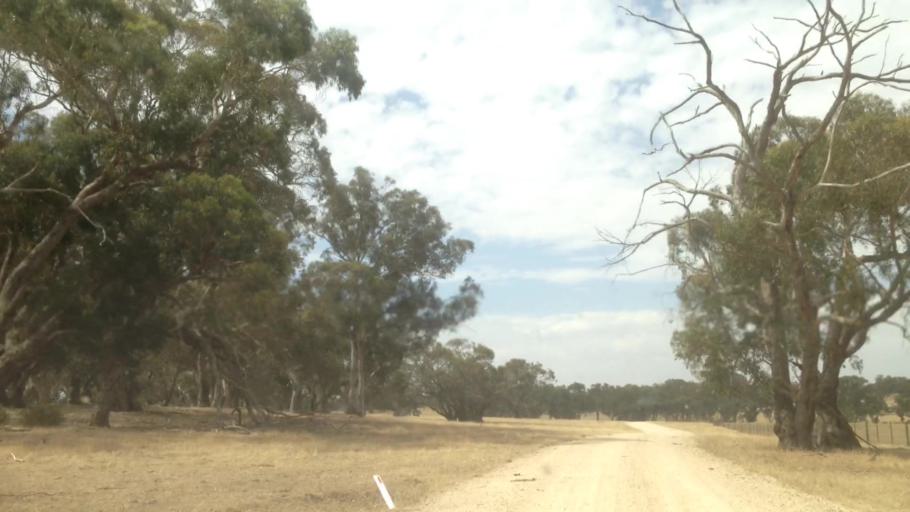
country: AU
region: South Australia
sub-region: Barossa
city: Williamstown
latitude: -34.7063
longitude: 138.9865
